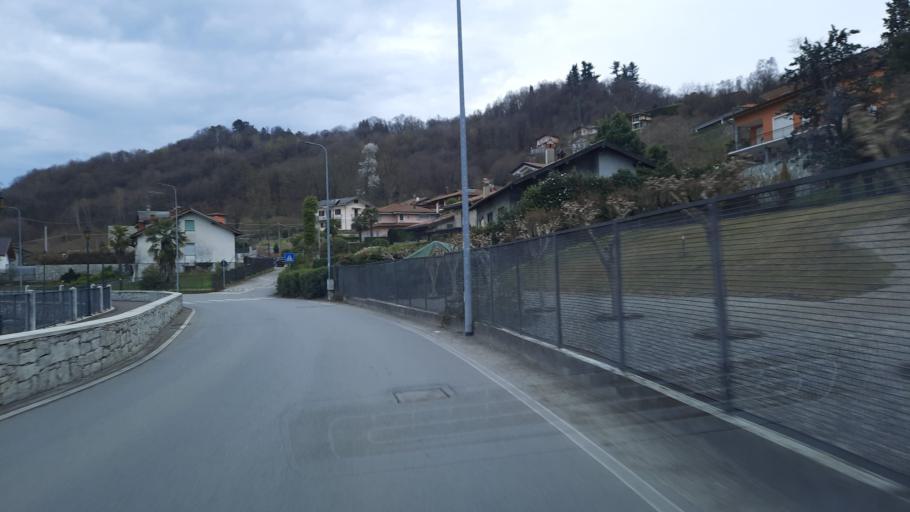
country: IT
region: Piedmont
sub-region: Provincia di Novara
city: Pella
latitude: 45.7908
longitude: 8.3841
